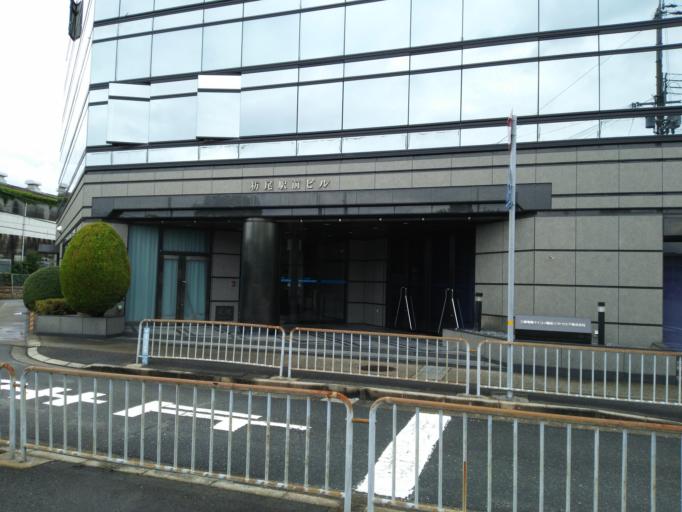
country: JP
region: Hyogo
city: Itami
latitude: 34.7647
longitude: 135.4227
